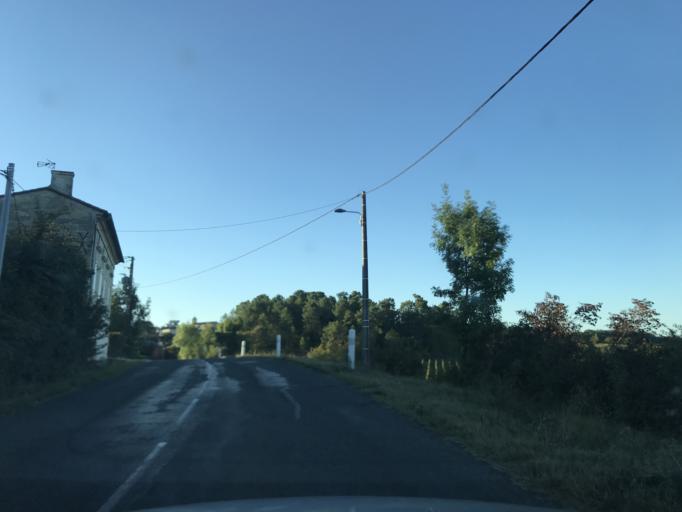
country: FR
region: Aquitaine
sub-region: Departement de la Gironde
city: Lussac
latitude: 44.9193
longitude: -0.0696
